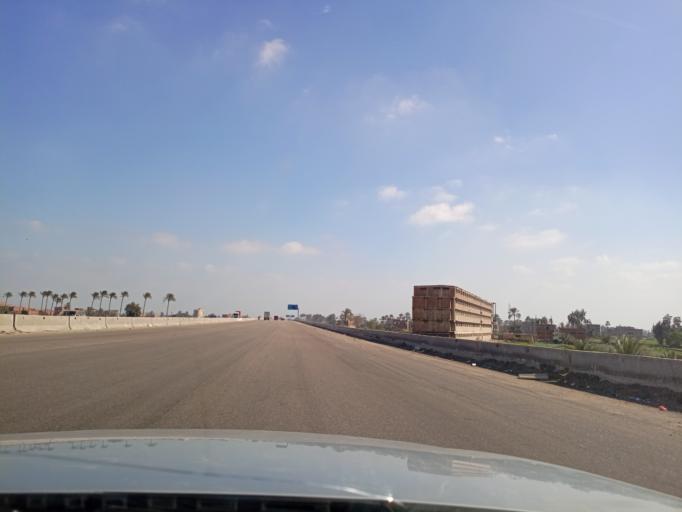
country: EG
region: Eastern Province
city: Mashtul as Suq
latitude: 30.4605
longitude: 31.3568
